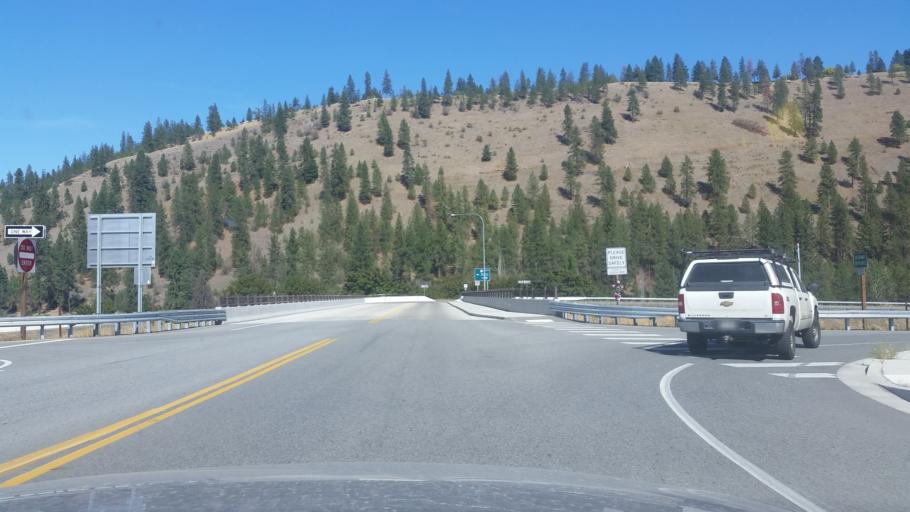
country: US
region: Washington
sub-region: Spokane County
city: Spokane
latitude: 47.6191
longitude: -117.4337
